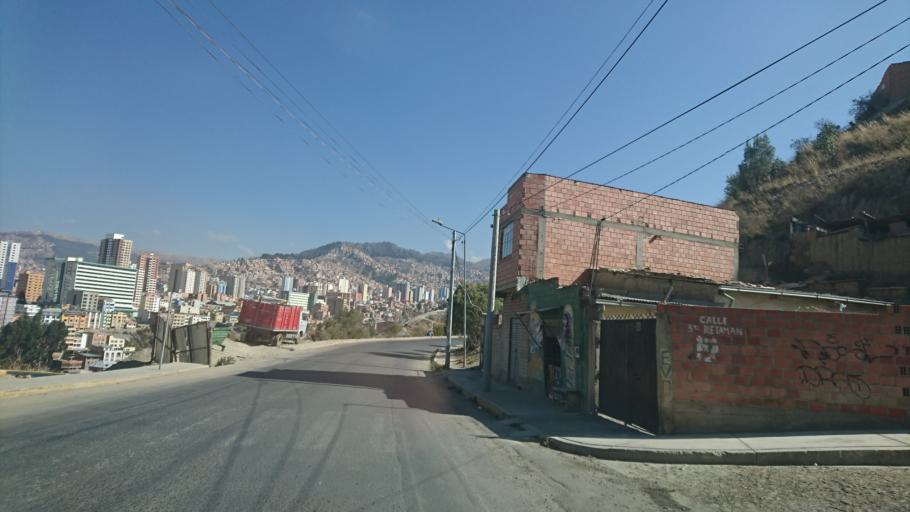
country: BO
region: La Paz
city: La Paz
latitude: -16.5045
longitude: -68.1127
